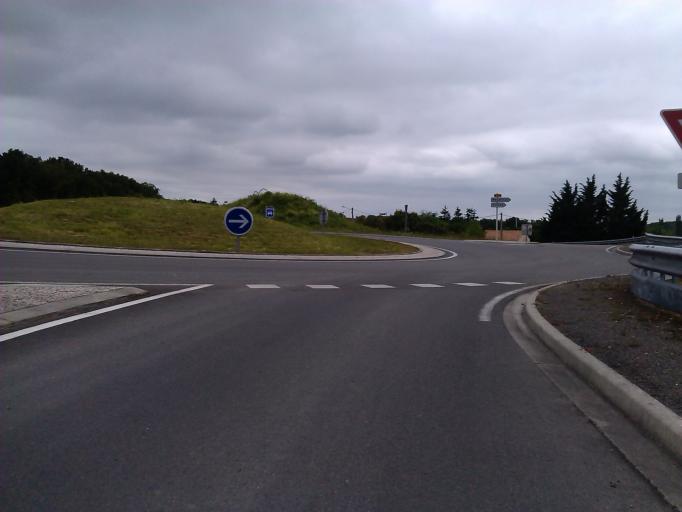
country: FR
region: Poitou-Charentes
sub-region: Departement de la Charente
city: Barbezieux-Saint-Hilaire
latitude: 45.5221
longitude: -0.0984
